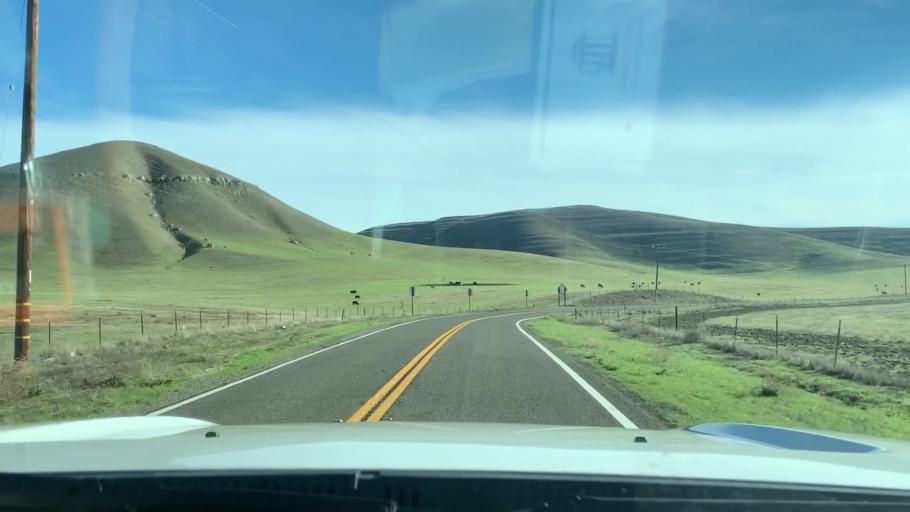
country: US
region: California
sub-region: Monterey County
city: King City
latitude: 36.1584
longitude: -120.9832
